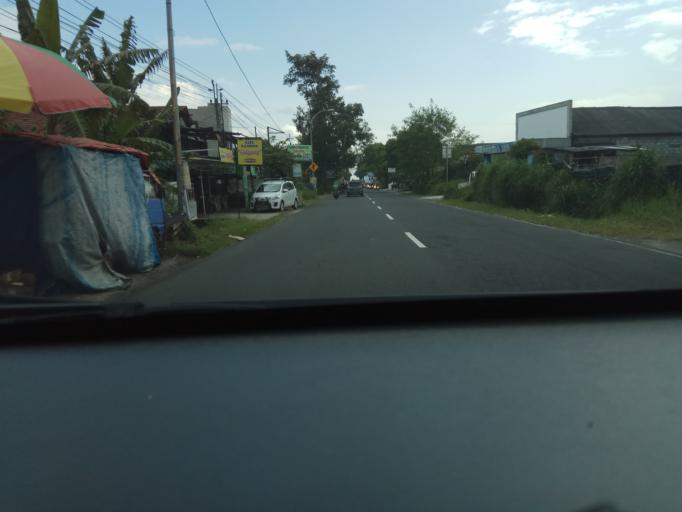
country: ID
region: Daerah Istimewa Yogyakarta
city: Melati
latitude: -7.7113
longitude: 110.4087
